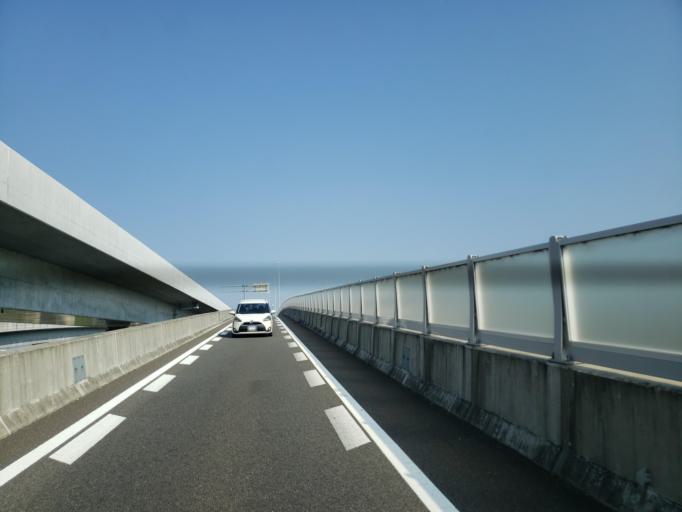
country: JP
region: Ehime
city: Masaki-cho
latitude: 33.8086
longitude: 132.7372
